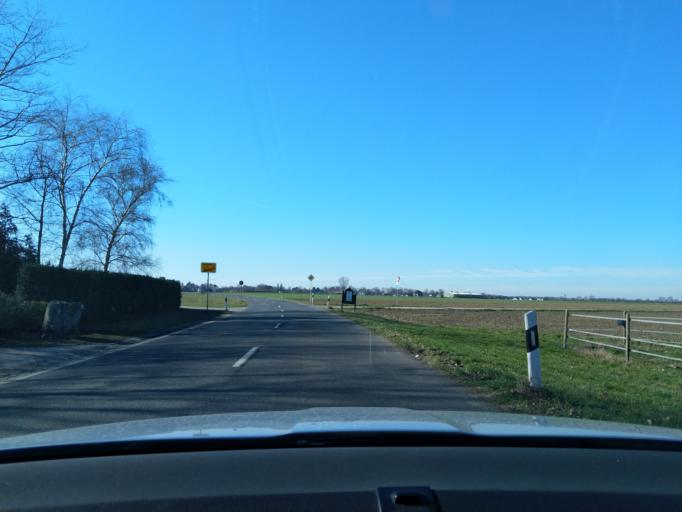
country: DE
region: North Rhine-Westphalia
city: Erkelenz
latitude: 51.1152
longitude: 6.3507
